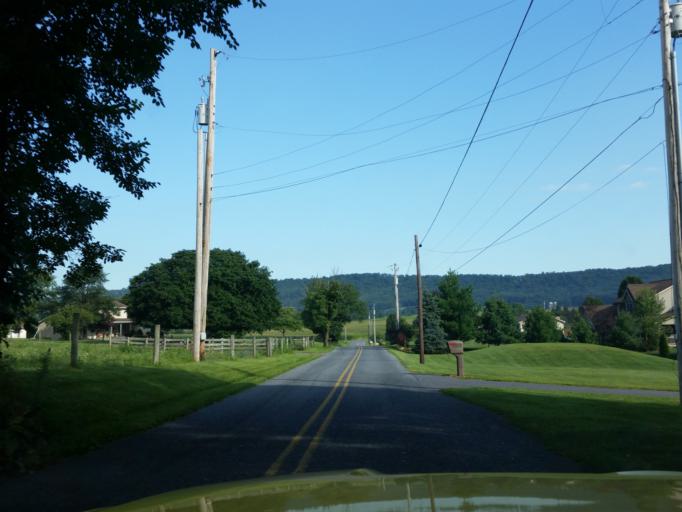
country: US
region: Pennsylvania
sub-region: Lebanon County
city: Fredericksburg
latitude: 40.4574
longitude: -76.4132
